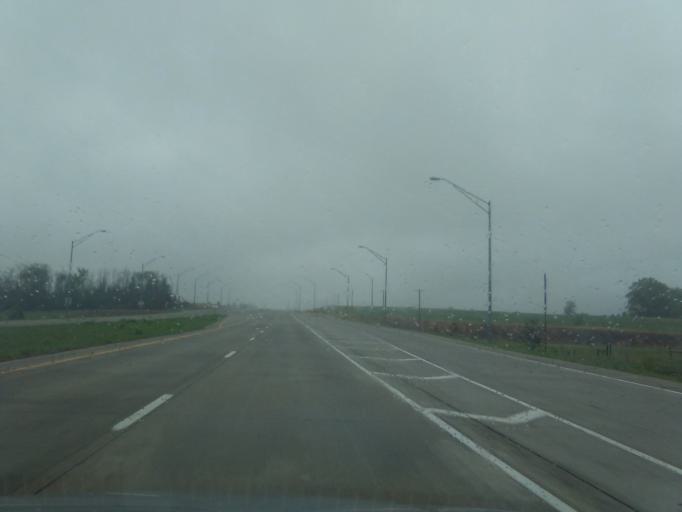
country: US
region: Nebraska
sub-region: Madison County
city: Norfolk
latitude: 42.0678
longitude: -97.3423
